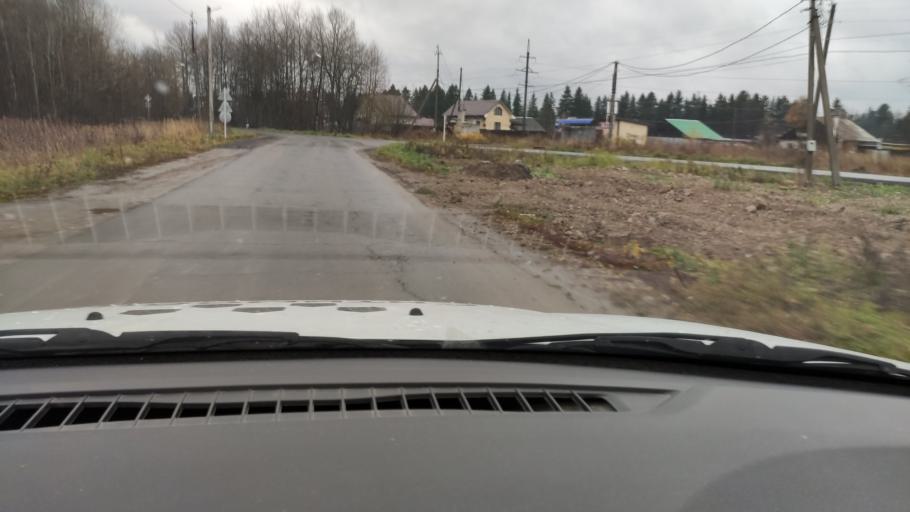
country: RU
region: Perm
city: Sylva
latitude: 58.0356
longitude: 56.7400
